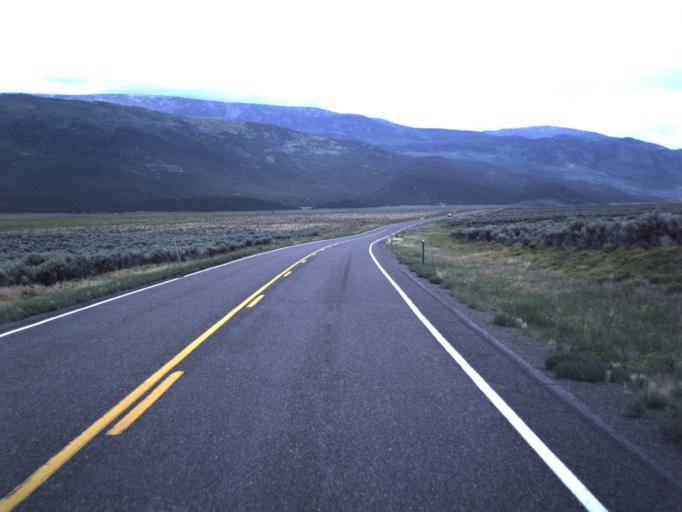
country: US
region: Utah
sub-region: Sevier County
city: Richfield
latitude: 38.6739
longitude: -111.8415
